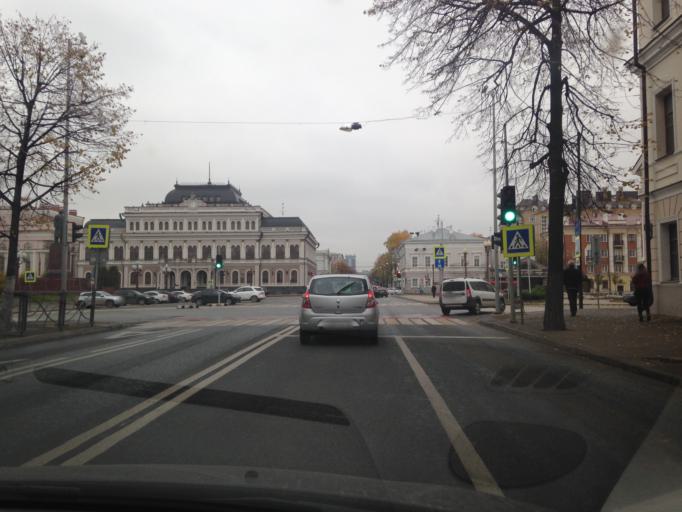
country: RU
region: Tatarstan
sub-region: Gorod Kazan'
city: Kazan
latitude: 55.7963
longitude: 49.1237
